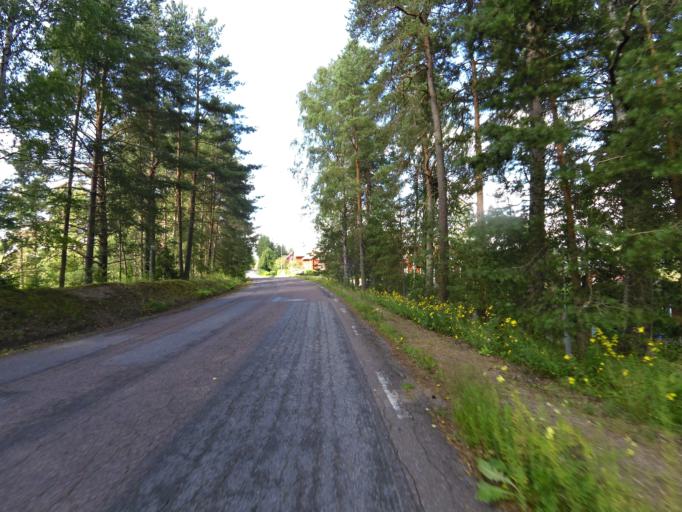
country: SE
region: Dalarna
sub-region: Faluns Kommun
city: Svardsjo
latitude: 60.6447
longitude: 15.8459
